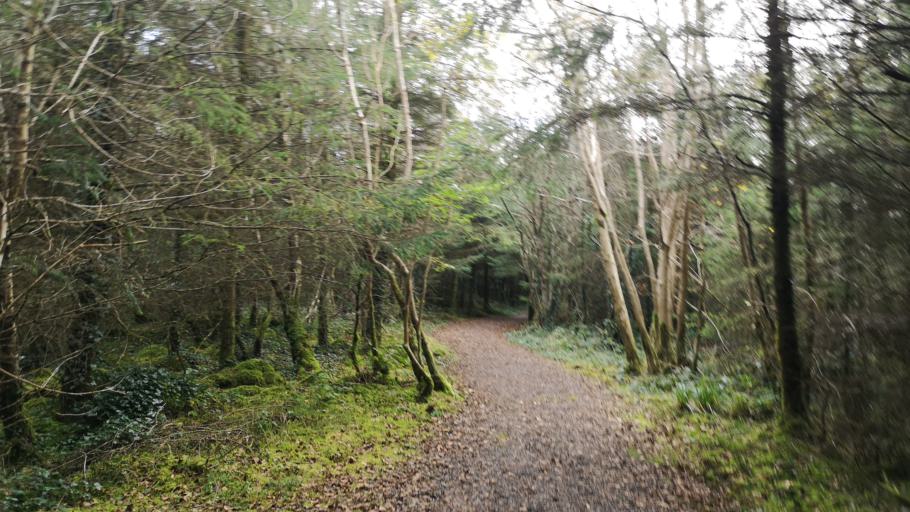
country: IE
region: Connaught
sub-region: County Galway
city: Loughrea
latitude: 53.2383
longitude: -8.6504
